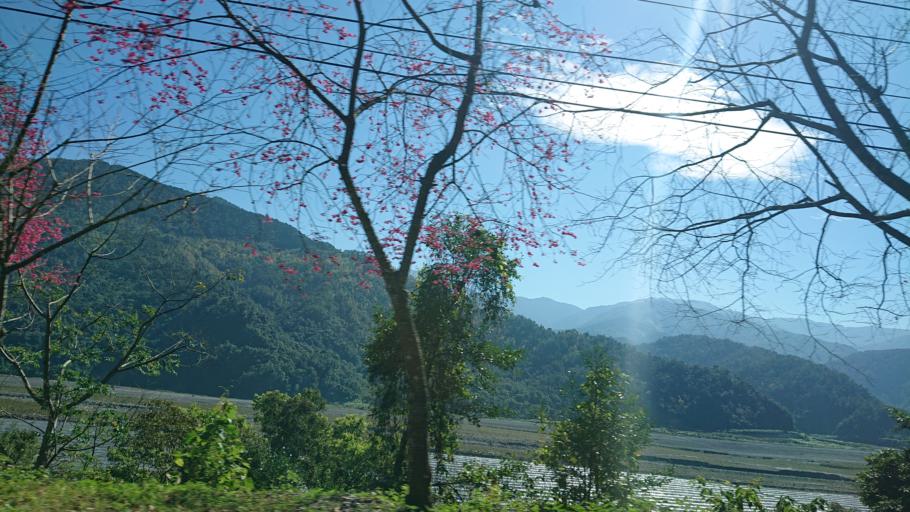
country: TW
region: Taiwan
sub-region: Yilan
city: Yilan
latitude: 24.5855
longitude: 121.4998
